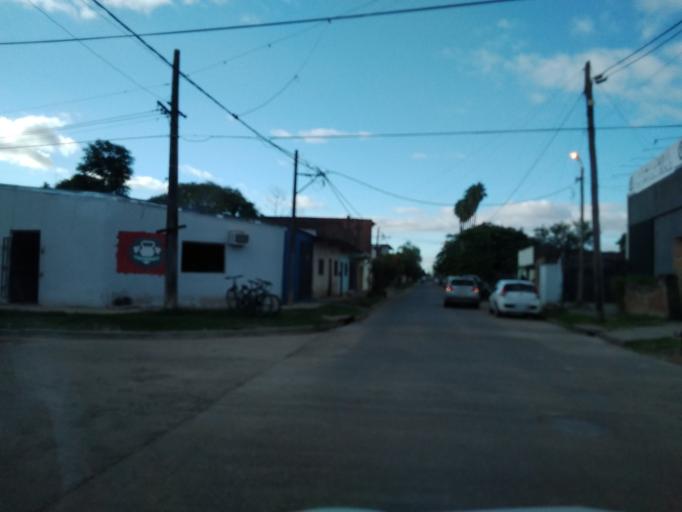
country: AR
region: Corrientes
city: Corrientes
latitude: -27.4784
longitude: -58.8062
